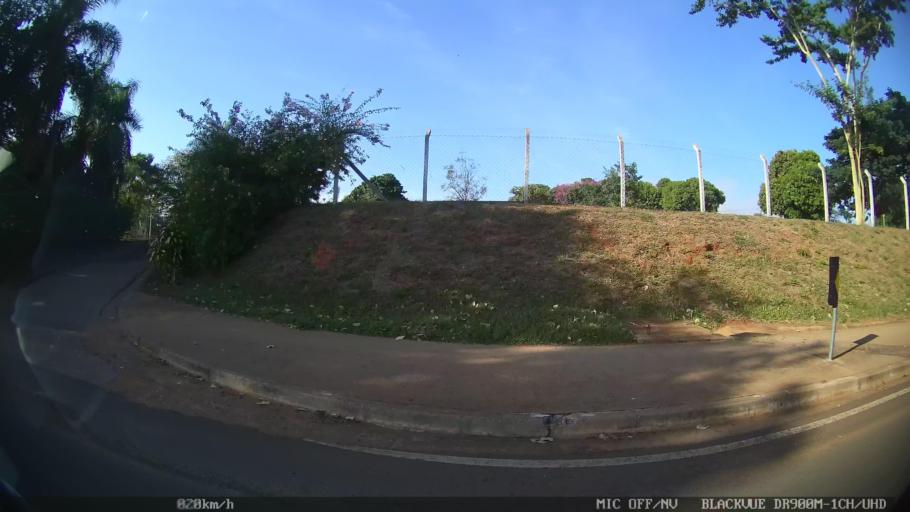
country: BR
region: Sao Paulo
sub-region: Sao Jose Do Rio Preto
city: Sao Jose do Rio Preto
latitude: -20.8122
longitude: -49.3546
